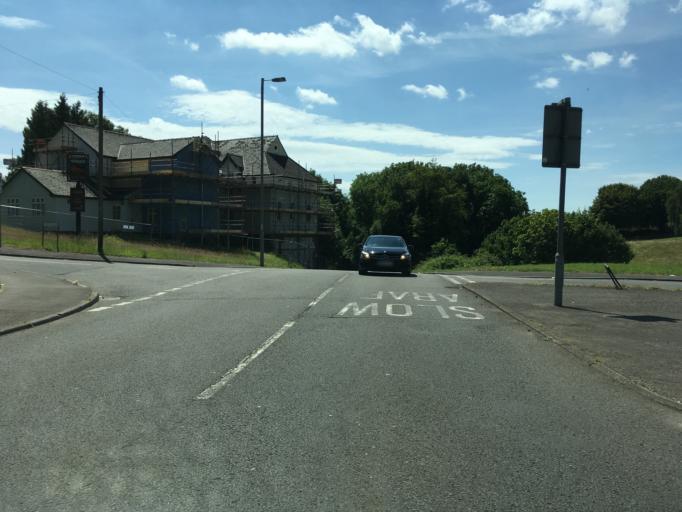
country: GB
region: Wales
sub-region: Newport
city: Newport
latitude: 51.5767
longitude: -3.0191
